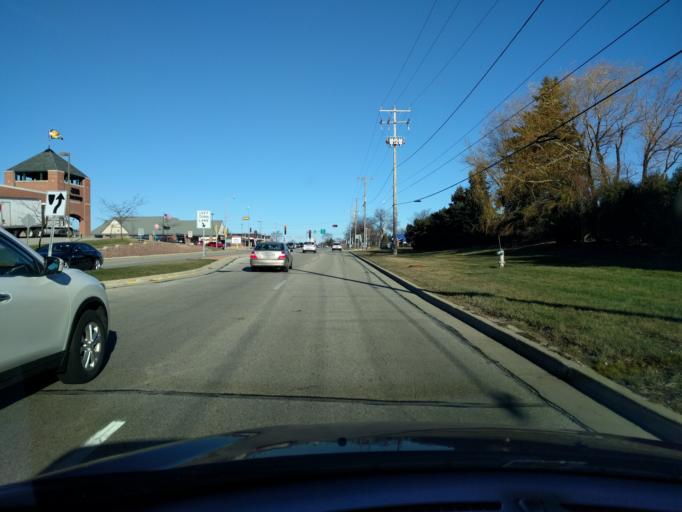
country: US
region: Wisconsin
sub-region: Milwaukee County
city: River Hills
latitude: 43.1740
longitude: -87.9125
